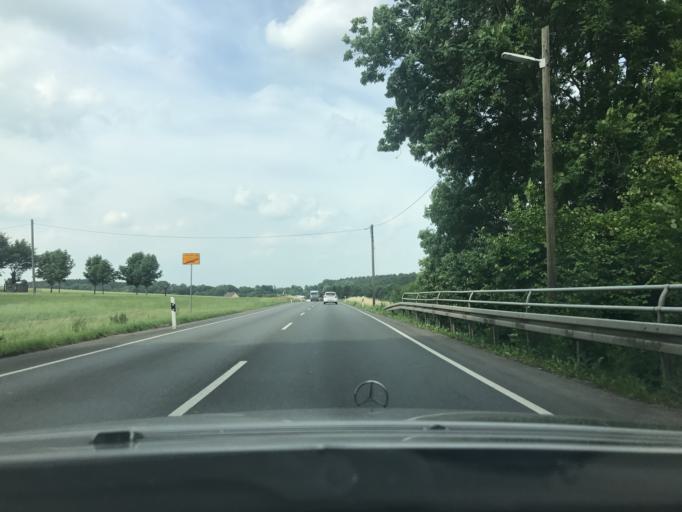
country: DE
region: North Rhine-Westphalia
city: Iserlohn
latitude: 51.4288
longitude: 7.6771
